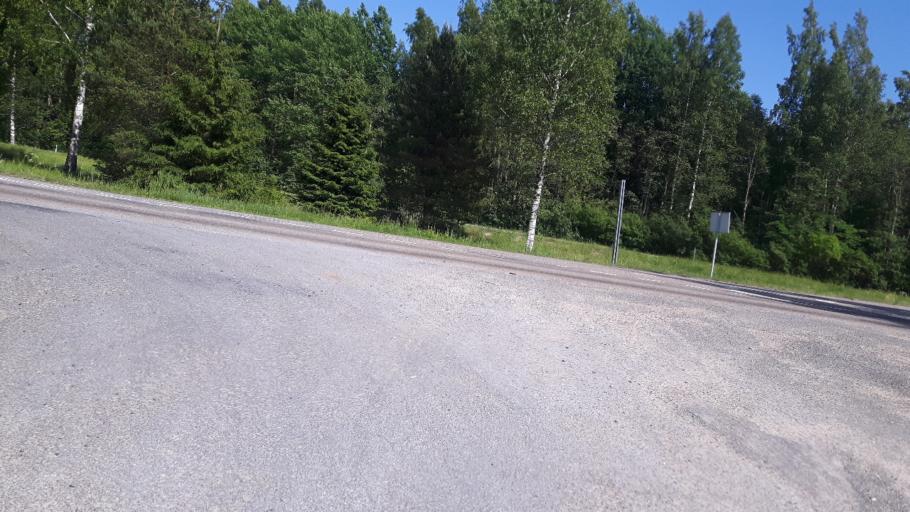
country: EE
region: Paernumaa
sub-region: Paikuse vald
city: Paikuse
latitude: 58.3911
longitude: 24.6411
